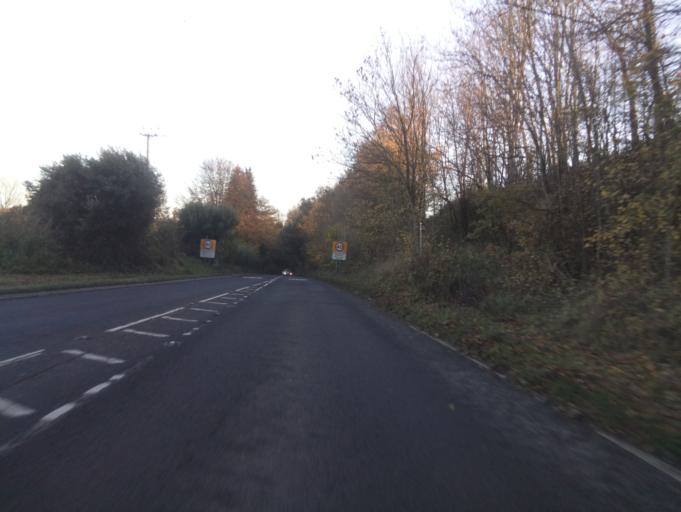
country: GB
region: England
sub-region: Wiltshire
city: Warminster
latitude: 51.1722
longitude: -2.1940
